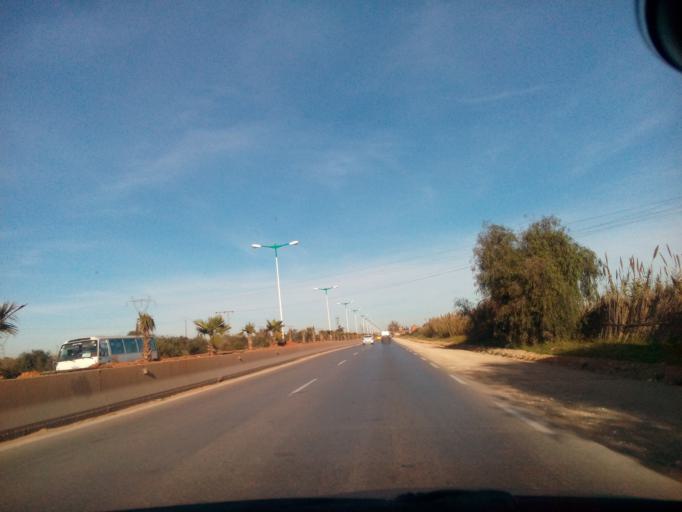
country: DZ
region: Mostaganem
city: Mostaganem
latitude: 35.8724
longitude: 0.1476
